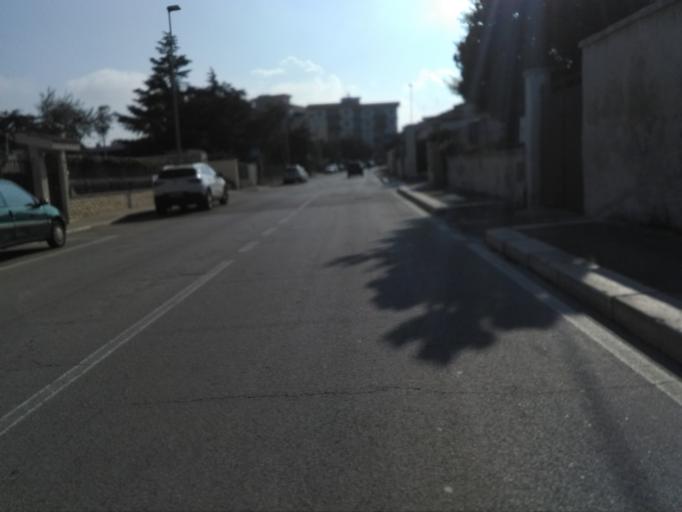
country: IT
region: Apulia
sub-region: Provincia di Bari
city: San Paolo
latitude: 41.1572
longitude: 16.7619
